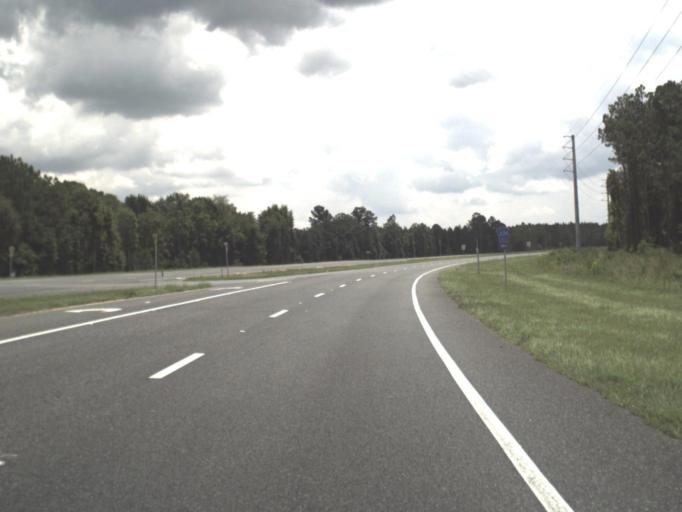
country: US
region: Florida
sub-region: Levy County
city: Bronson
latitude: 29.4766
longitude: -82.6855
